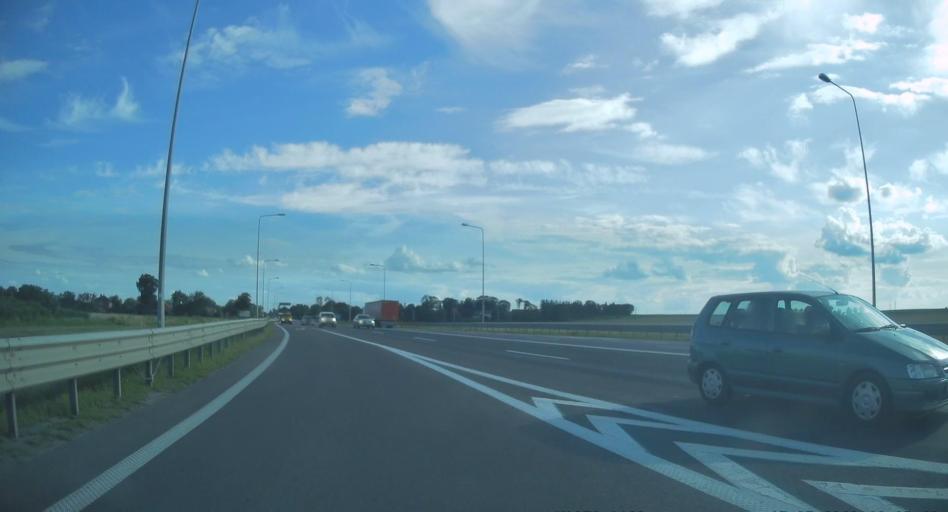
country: PL
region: Subcarpathian Voivodeship
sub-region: Powiat przemyski
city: Orly
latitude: 49.9053
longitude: 22.8176
